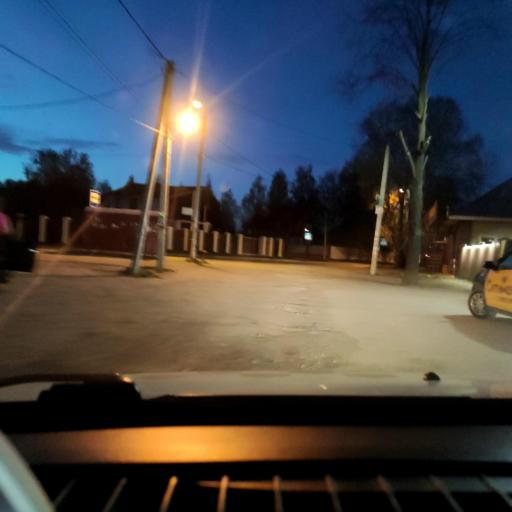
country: RU
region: Perm
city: Perm
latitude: 58.0480
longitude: 56.3379
